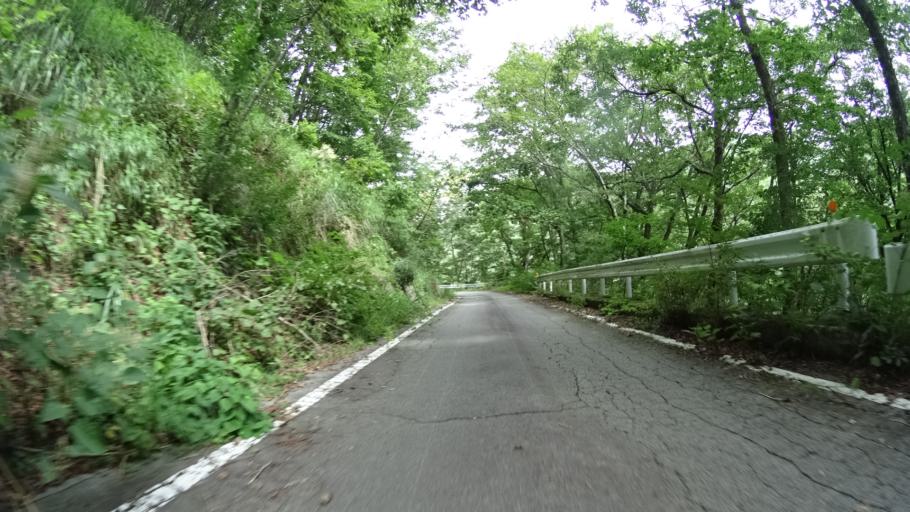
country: JP
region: Yamanashi
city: Nirasaki
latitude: 35.8063
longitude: 138.5424
